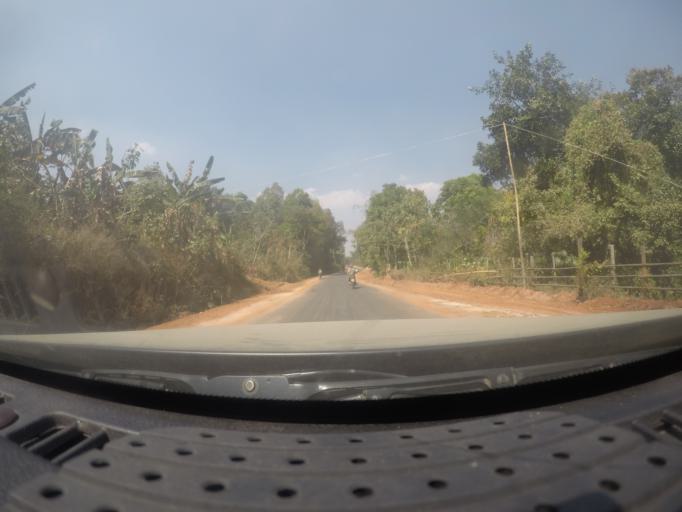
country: MM
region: Shan
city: Taunggyi
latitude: 21.0815
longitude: 96.4969
